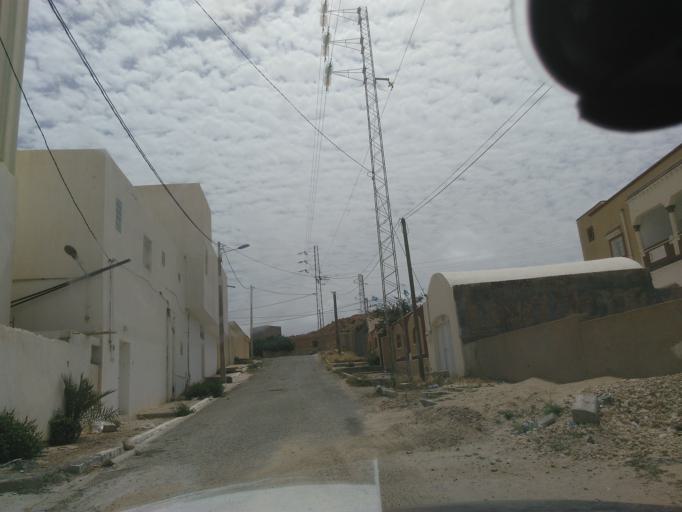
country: TN
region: Tataouine
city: Tataouine
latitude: 32.9455
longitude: 10.4651
